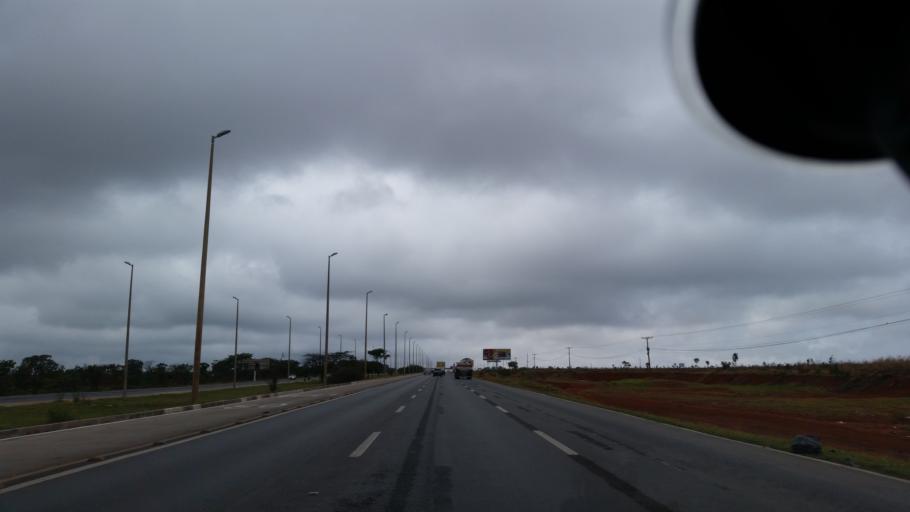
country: BR
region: Federal District
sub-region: Brasilia
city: Brasilia
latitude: -15.9608
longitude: -47.9933
